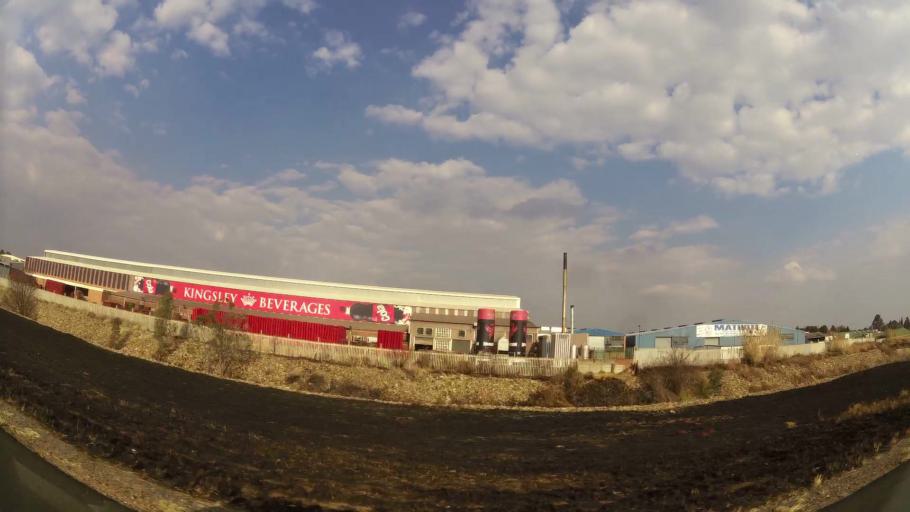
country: ZA
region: Gauteng
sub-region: Ekurhuleni Metropolitan Municipality
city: Springs
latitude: -26.2790
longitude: 28.4546
